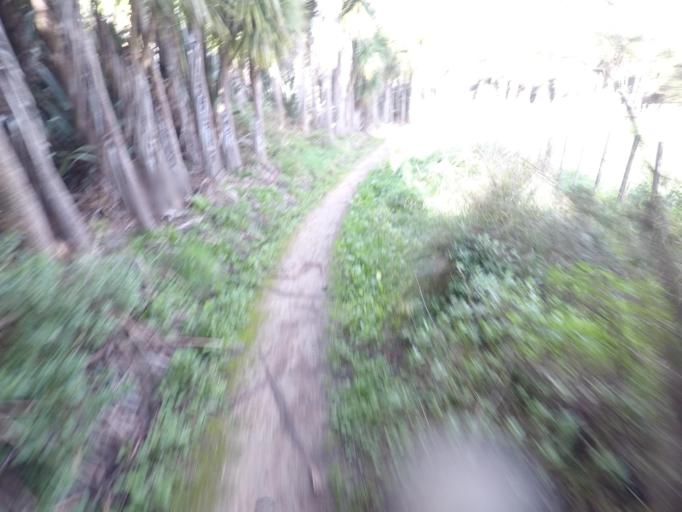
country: NZ
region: Auckland
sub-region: Auckland
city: Manukau City
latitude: -36.9985
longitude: 174.9145
